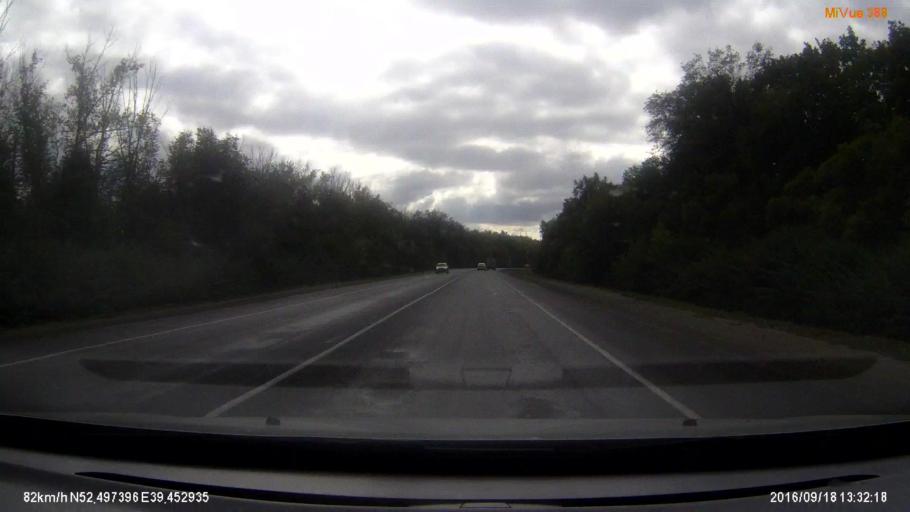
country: RU
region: Lipetsk
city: Borinskoye
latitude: 52.4627
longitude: 39.3902
